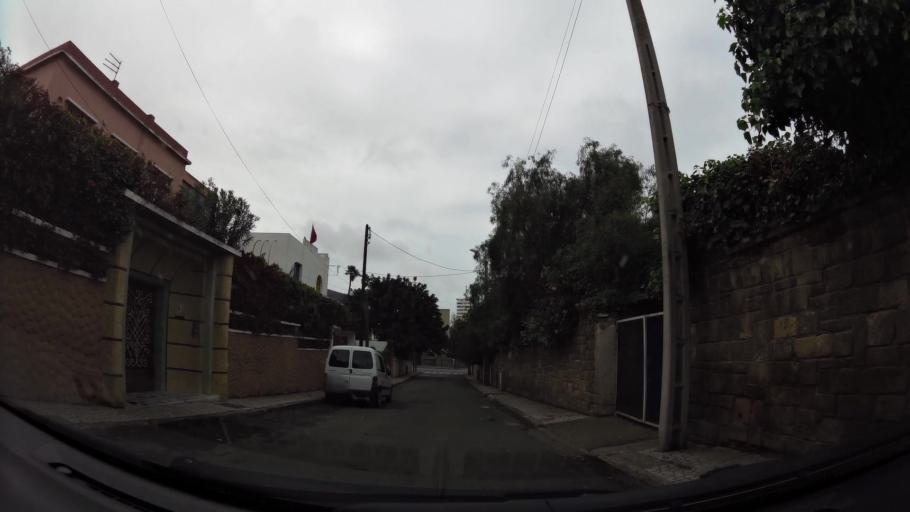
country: MA
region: Grand Casablanca
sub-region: Casablanca
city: Casablanca
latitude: 33.5813
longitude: -7.6063
